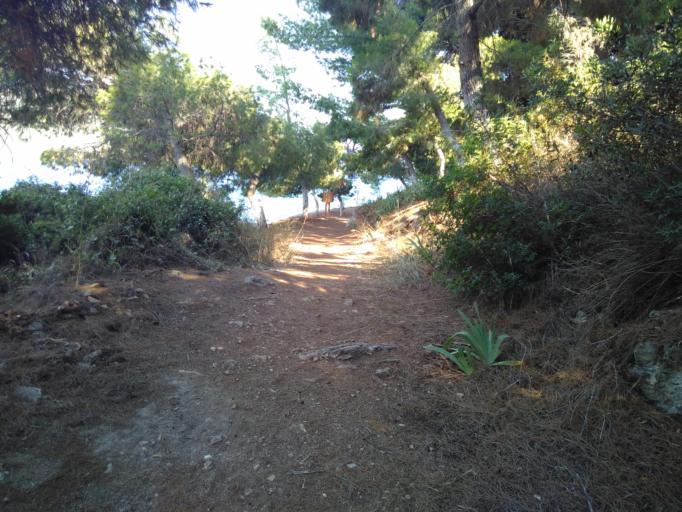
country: GR
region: West Greece
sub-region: Nomos Achaias
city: Selianitika
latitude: 38.3726
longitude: 22.0778
